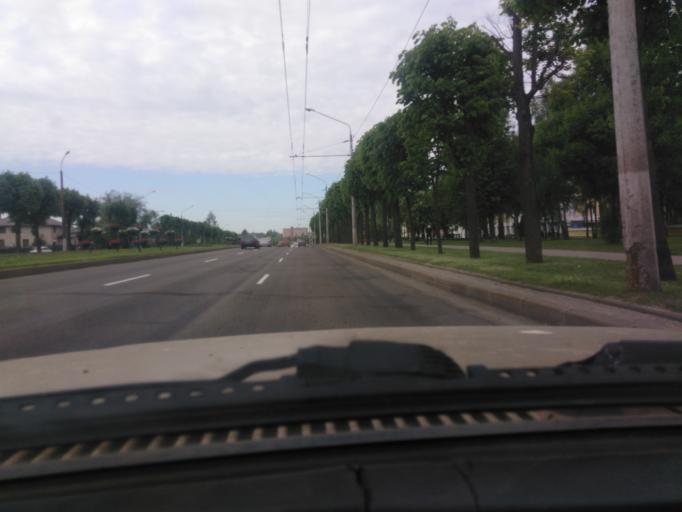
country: BY
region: Mogilev
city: Mahilyow
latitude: 53.9041
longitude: 30.3034
